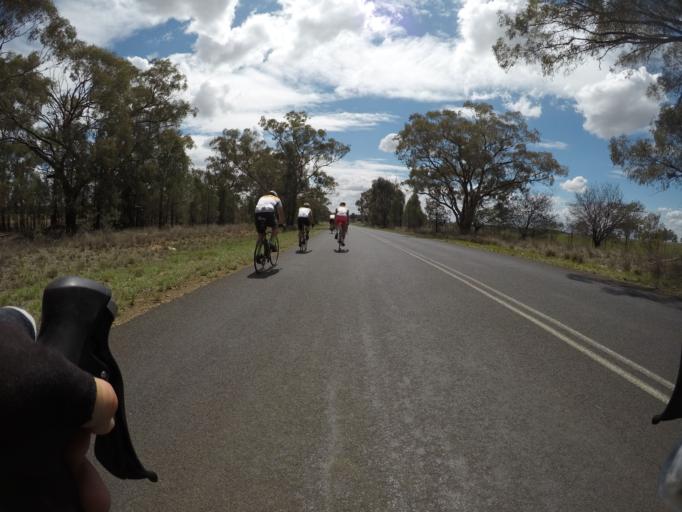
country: AU
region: New South Wales
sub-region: Dubbo Municipality
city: Dubbo
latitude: -32.2974
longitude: 148.5995
